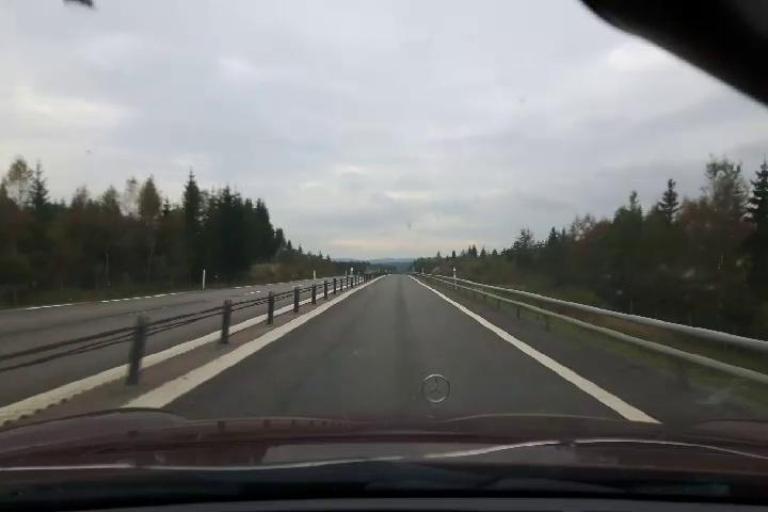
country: SE
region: Vaesternorrland
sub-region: Haernoesands Kommun
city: Haernoesand
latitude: 62.7165
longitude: 17.9100
